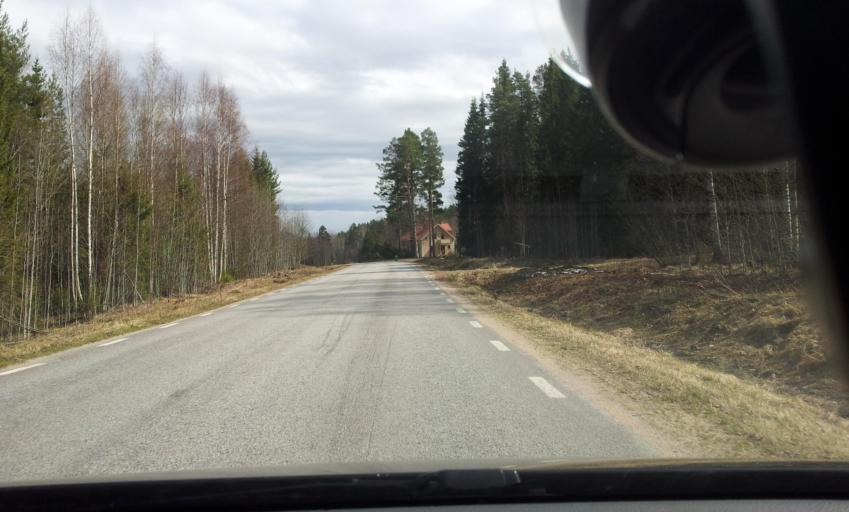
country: SE
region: Gaevleborg
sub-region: Ljusdals Kommun
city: Ljusdal
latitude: 61.7682
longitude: 16.0237
